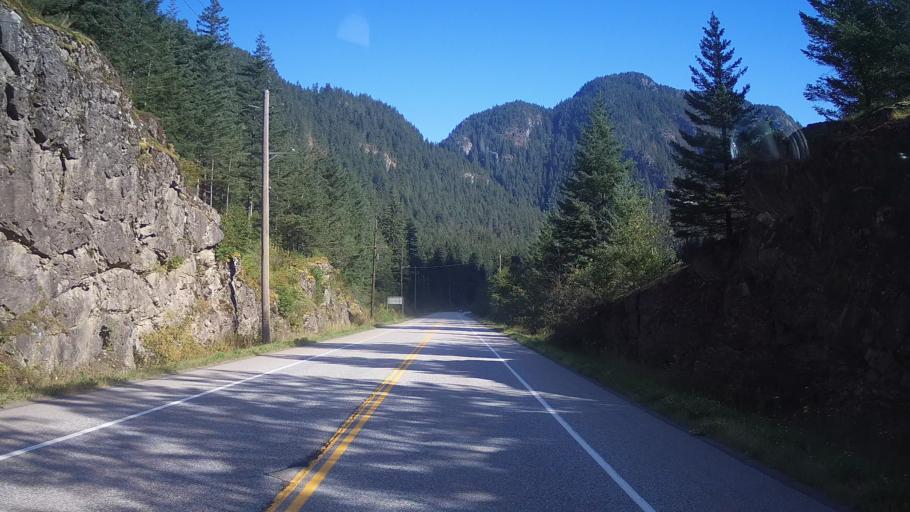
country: CA
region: British Columbia
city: Hope
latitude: 49.5980
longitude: -121.4144
